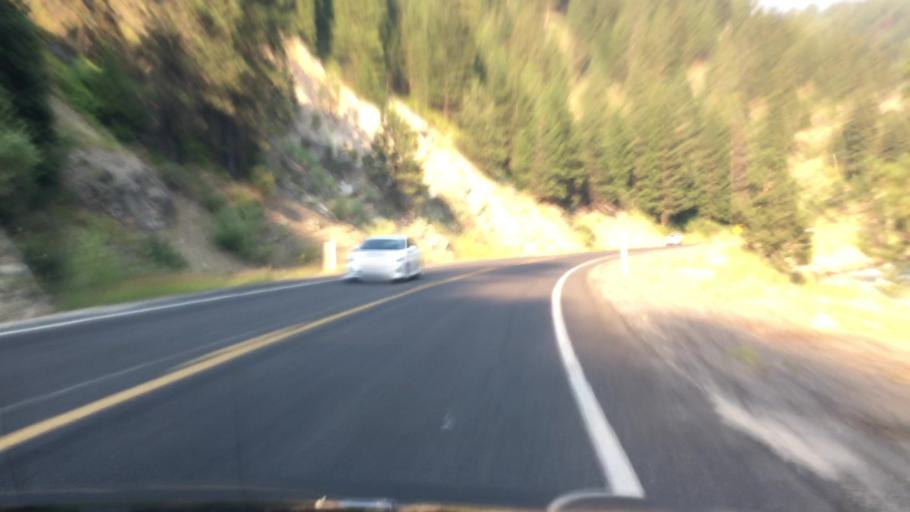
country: US
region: Idaho
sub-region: Valley County
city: Cascade
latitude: 44.2633
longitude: -116.0757
